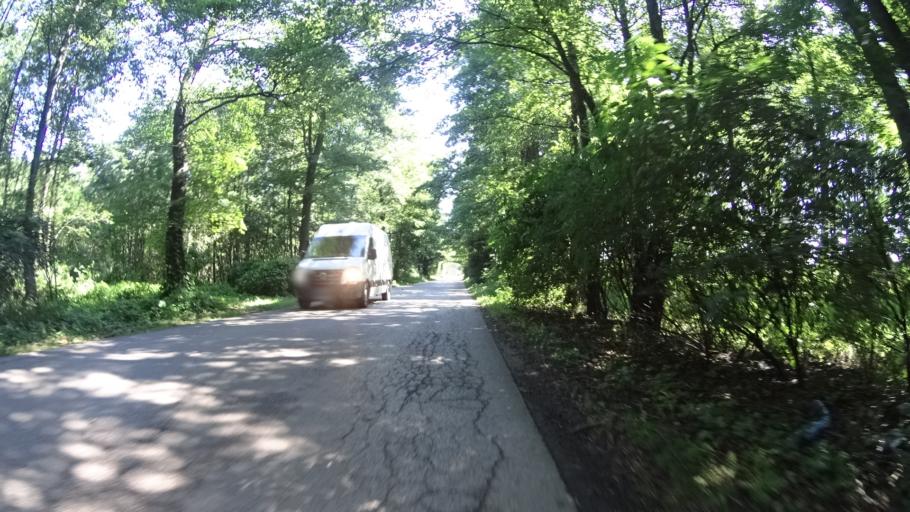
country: PL
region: Masovian Voivodeship
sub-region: Powiat bialobrzeski
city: Wysmierzyce
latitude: 51.6620
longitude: 20.8370
